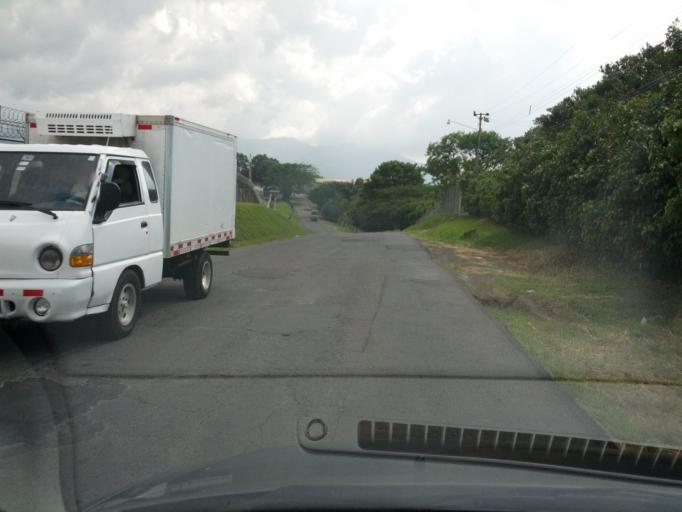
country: CR
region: Alajuela
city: Alajuela
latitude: 9.9899
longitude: -84.2240
